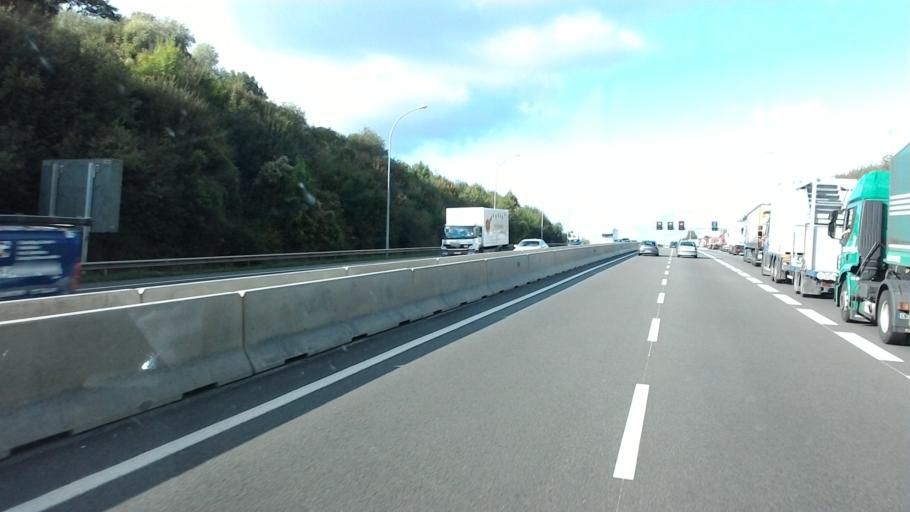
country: LU
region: Luxembourg
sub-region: Canton d'Esch-sur-Alzette
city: Dudelange
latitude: 49.4740
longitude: 6.1214
